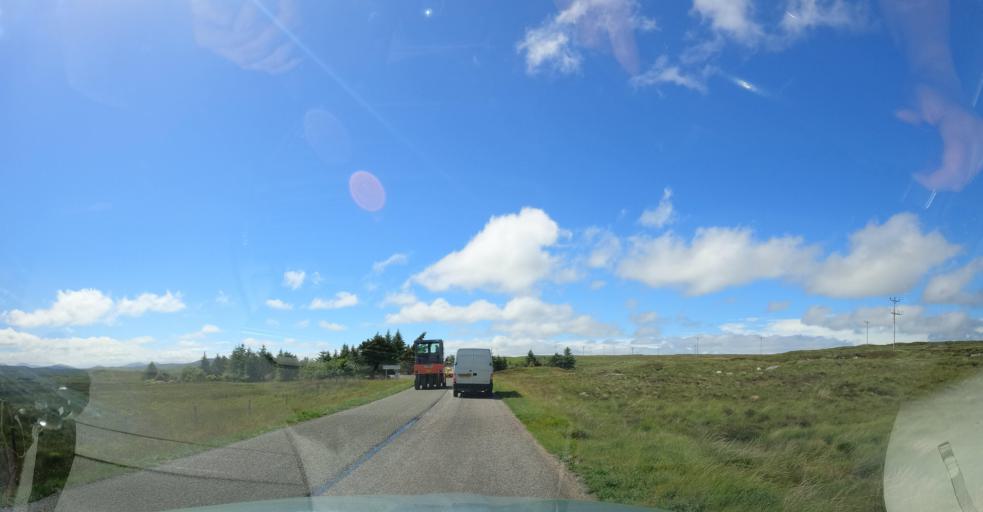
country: GB
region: Scotland
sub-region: Eilean Siar
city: Harris
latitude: 58.1881
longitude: -6.6969
